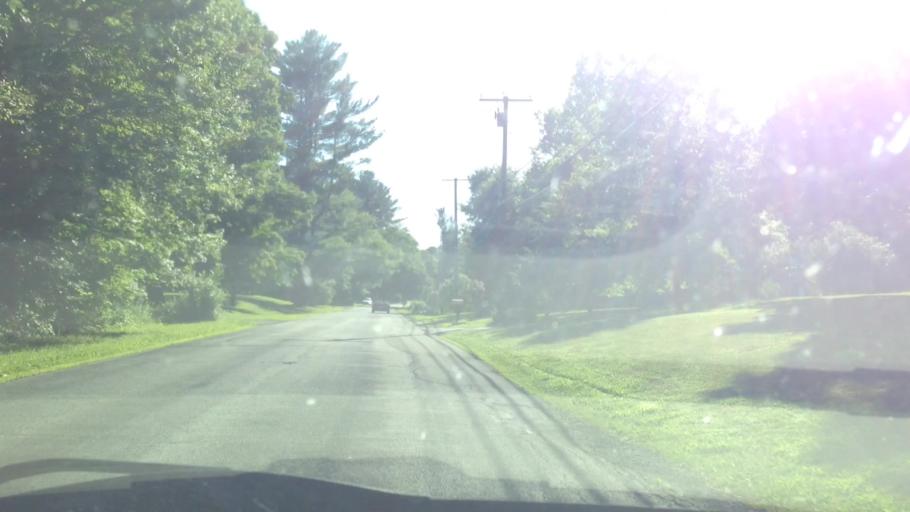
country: US
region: New York
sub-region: Ulster County
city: New Paltz
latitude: 41.7420
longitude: -74.0503
